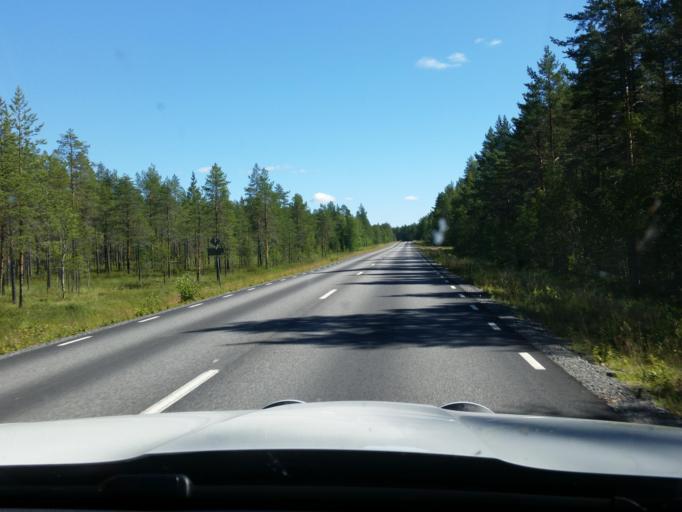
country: SE
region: Norrbotten
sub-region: Pitea Kommun
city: Roknas
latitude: 65.3423
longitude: 20.9544
